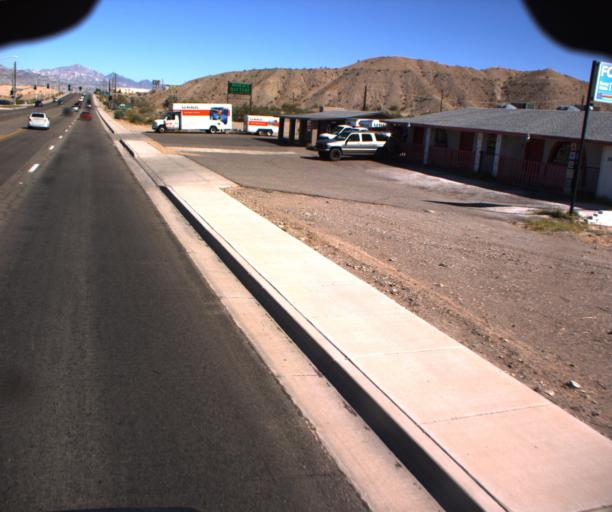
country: US
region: Arizona
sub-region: Mohave County
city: Bullhead City
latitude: 35.0747
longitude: -114.5921
